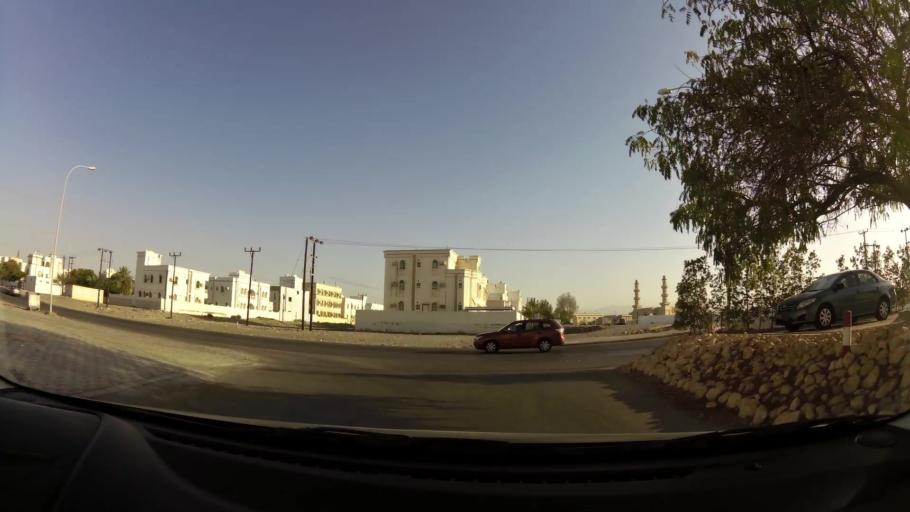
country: OM
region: Muhafazat Masqat
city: As Sib al Jadidah
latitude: 23.6325
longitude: 58.1921
